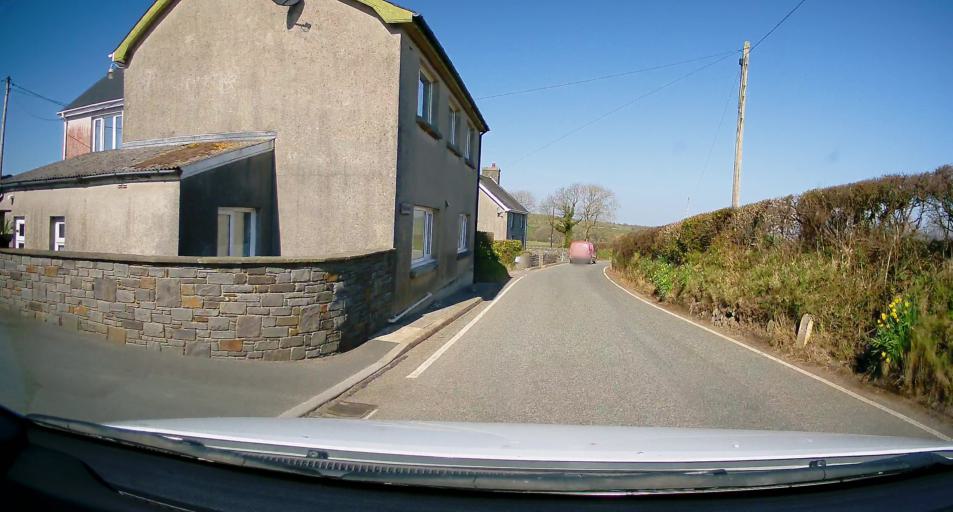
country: GB
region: Wales
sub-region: County of Ceredigion
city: Lledrod
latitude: 52.3082
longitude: -4.0642
